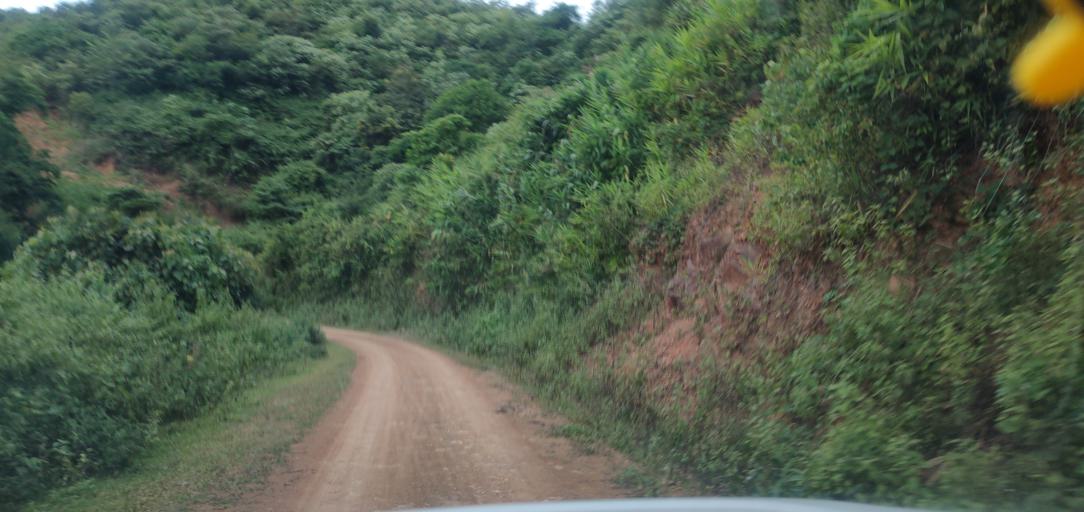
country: LA
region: Phongsali
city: Khoa
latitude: 21.2004
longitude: 102.2818
